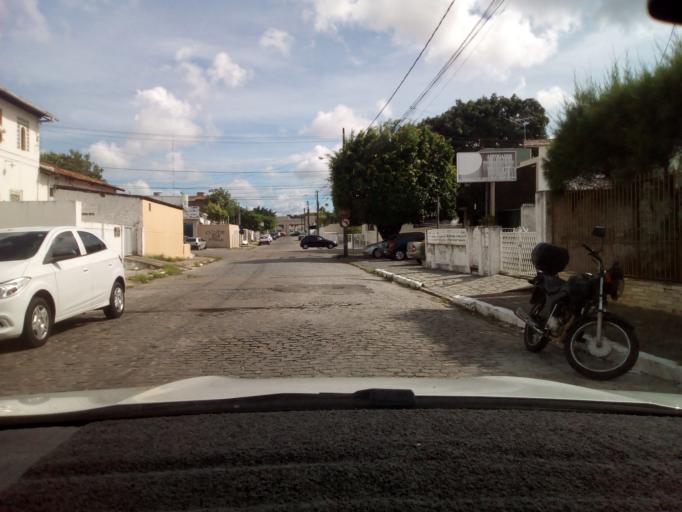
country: BR
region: Paraiba
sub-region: Joao Pessoa
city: Joao Pessoa
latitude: -7.1250
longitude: -34.8708
